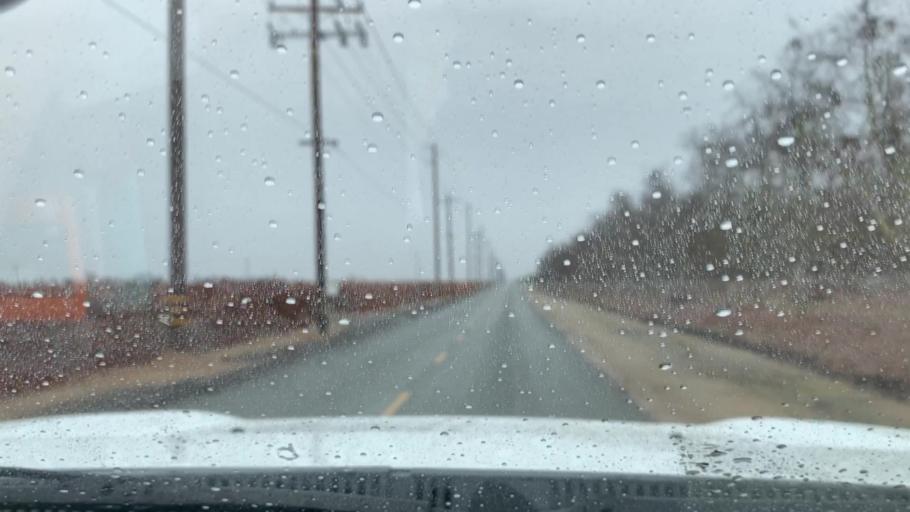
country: US
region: California
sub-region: Tulare County
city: Richgrove
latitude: 35.8341
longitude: -119.1815
